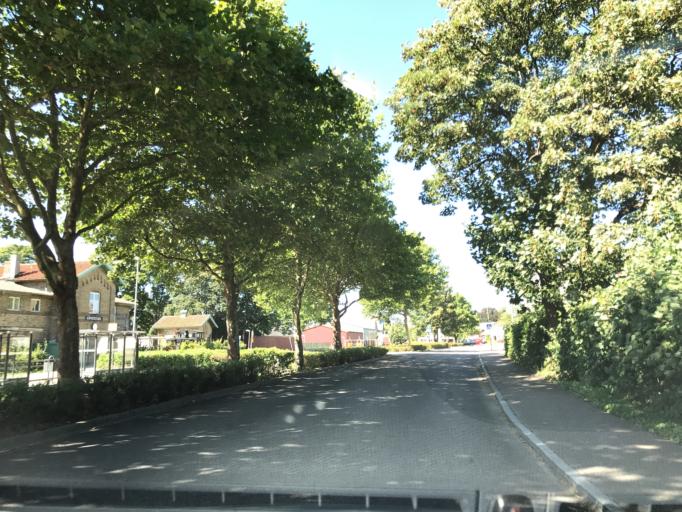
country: SE
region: Skane
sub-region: Tomelilla Kommun
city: Tomelilla
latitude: 55.6536
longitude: 13.8919
